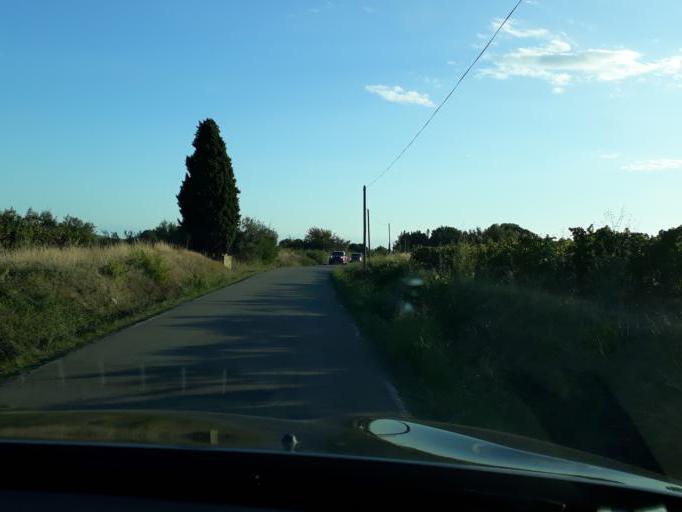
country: FR
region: Languedoc-Roussillon
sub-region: Departement de l'Herault
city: Pomerols
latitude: 43.3673
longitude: 3.4948
